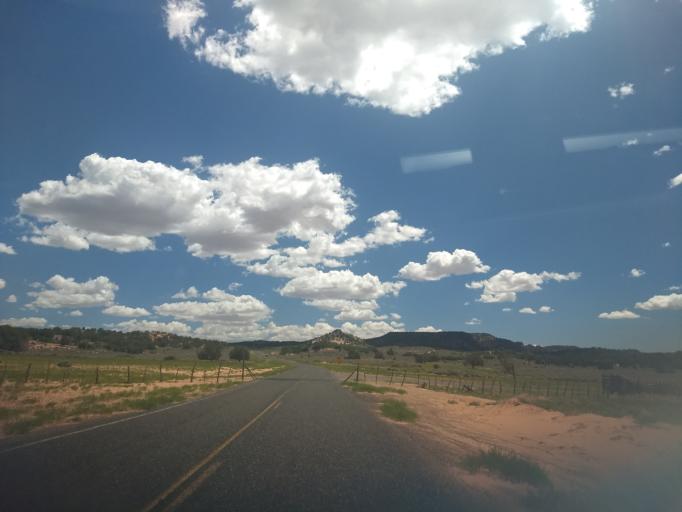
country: US
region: Utah
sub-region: Kane County
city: Kanab
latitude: 37.1472
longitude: -112.6738
